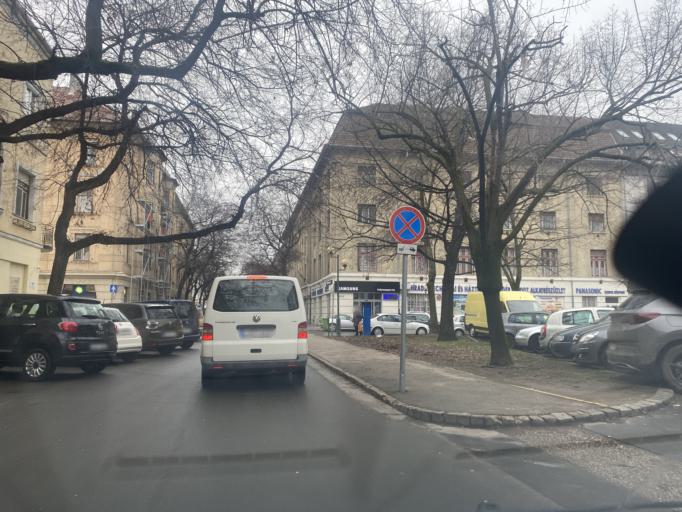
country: HU
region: Csongrad
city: Szeged
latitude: 46.2563
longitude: 20.1456
